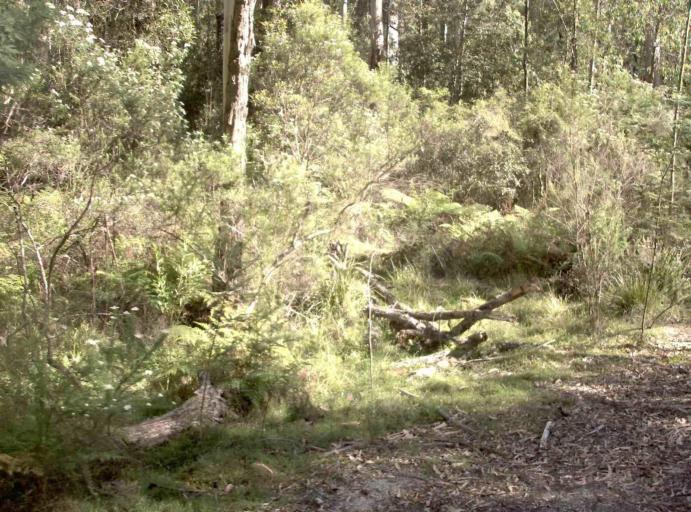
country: AU
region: Victoria
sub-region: East Gippsland
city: Lakes Entrance
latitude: -37.4659
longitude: 148.5631
